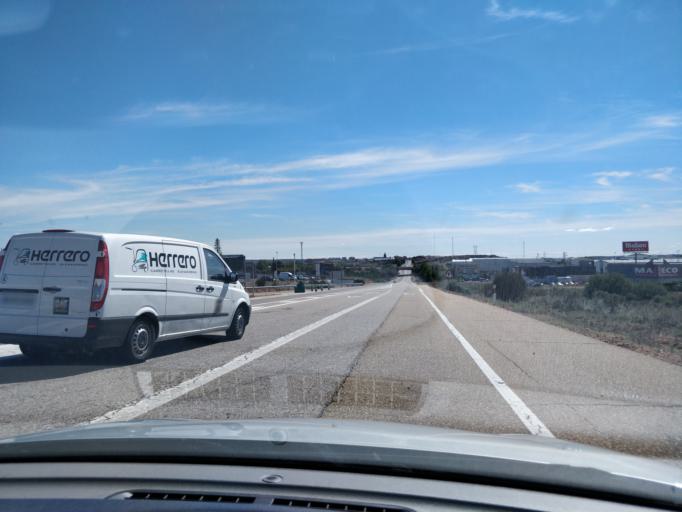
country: ES
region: Castille and Leon
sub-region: Provincia de Leon
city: Astorga
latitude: 42.4727
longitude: -6.0883
